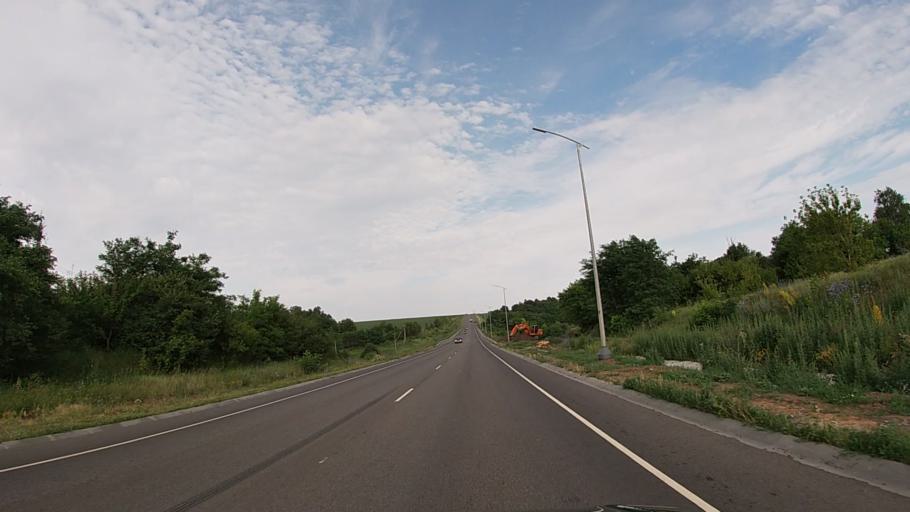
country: RU
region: Belgorod
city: Severnyy
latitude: 50.6644
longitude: 36.5222
